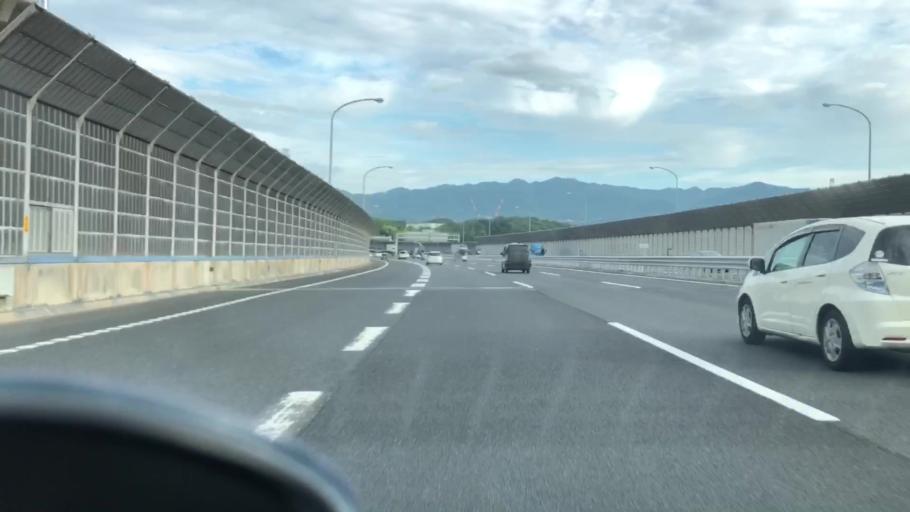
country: JP
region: Hyogo
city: Sandacho
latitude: 34.8434
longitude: 135.2269
